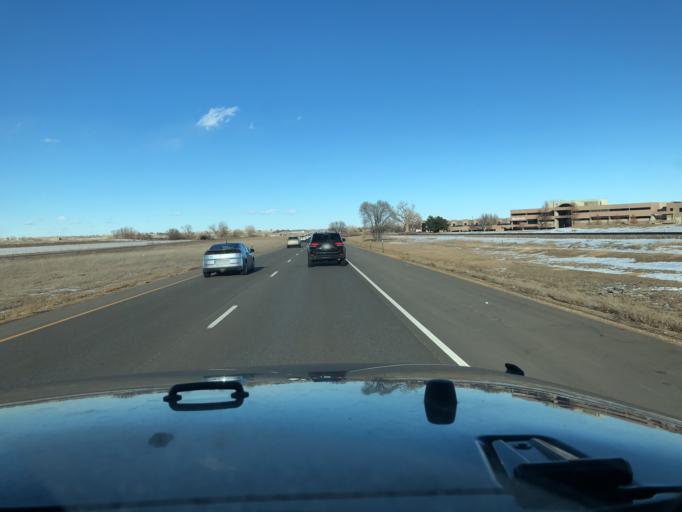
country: US
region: Colorado
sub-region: Boulder County
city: Gunbarrel
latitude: 40.0624
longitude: -105.2195
